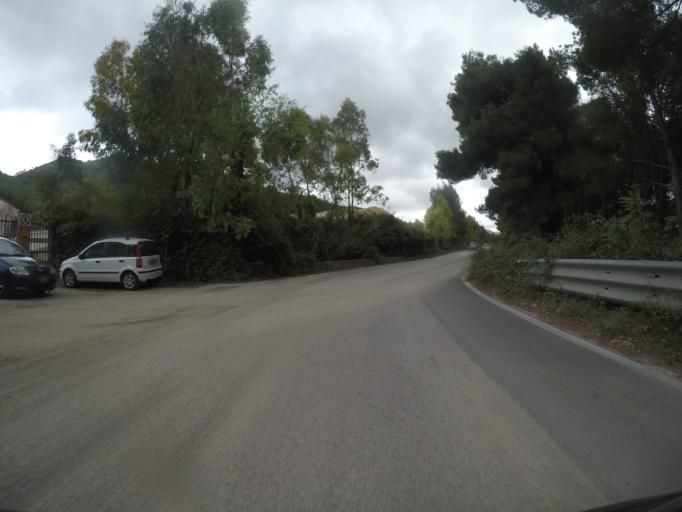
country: IT
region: Sicily
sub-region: Palermo
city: Montelepre
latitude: 38.1064
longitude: 13.1701
